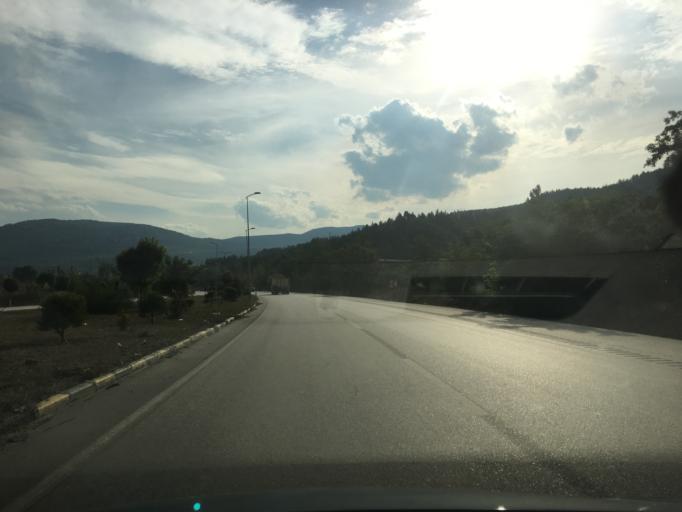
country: TR
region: Karabuk
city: Karabuk
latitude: 41.1189
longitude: 32.6743
